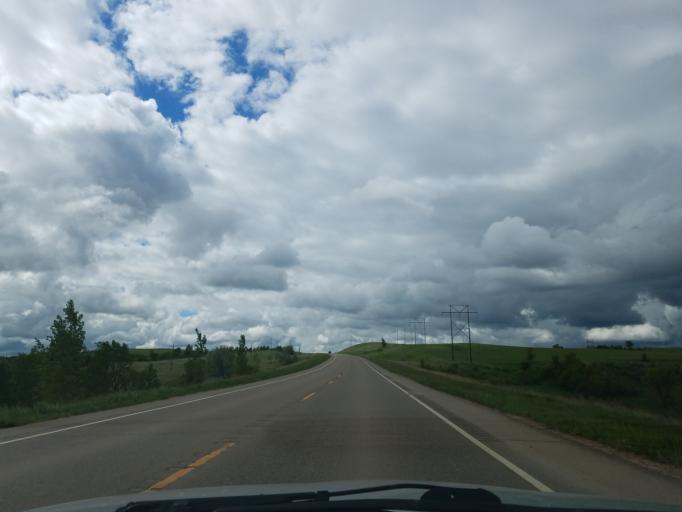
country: US
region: North Dakota
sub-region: McKenzie County
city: Watford City
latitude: 47.6792
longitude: -103.2841
